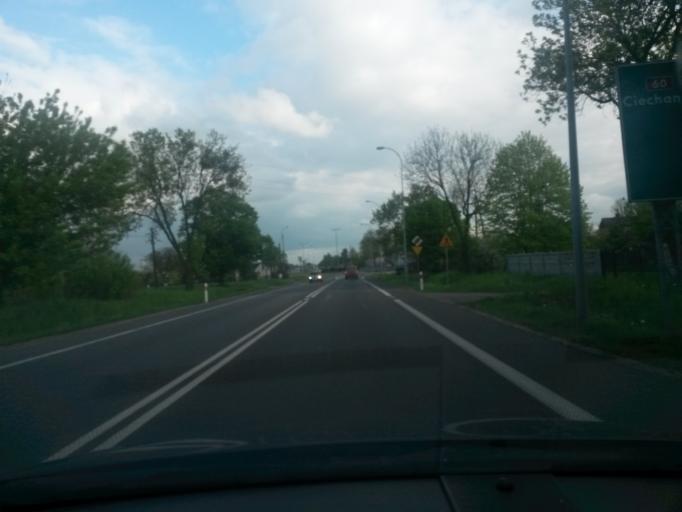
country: PL
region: Masovian Voivodeship
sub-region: Powiat plocki
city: Drobin
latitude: 52.7385
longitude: 19.9941
